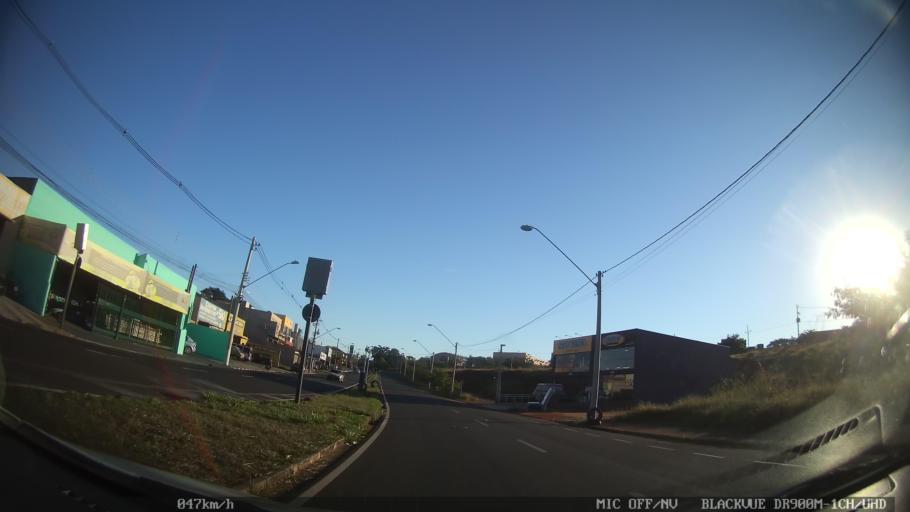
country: BR
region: Sao Paulo
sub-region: Sao Jose Do Rio Preto
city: Sao Jose do Rio Preto
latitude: -20.7920
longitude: -49.3515
